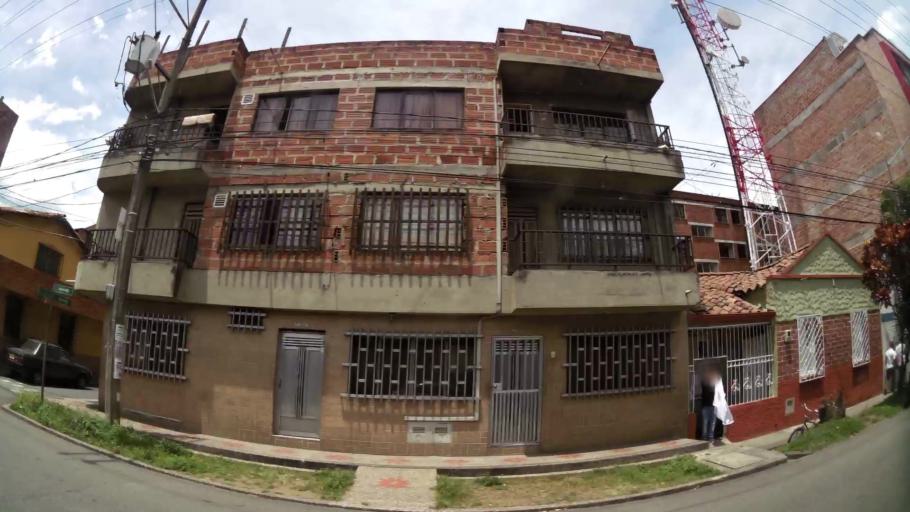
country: CO
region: Antioquia
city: Bello
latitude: 6.3307
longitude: -75.5554
